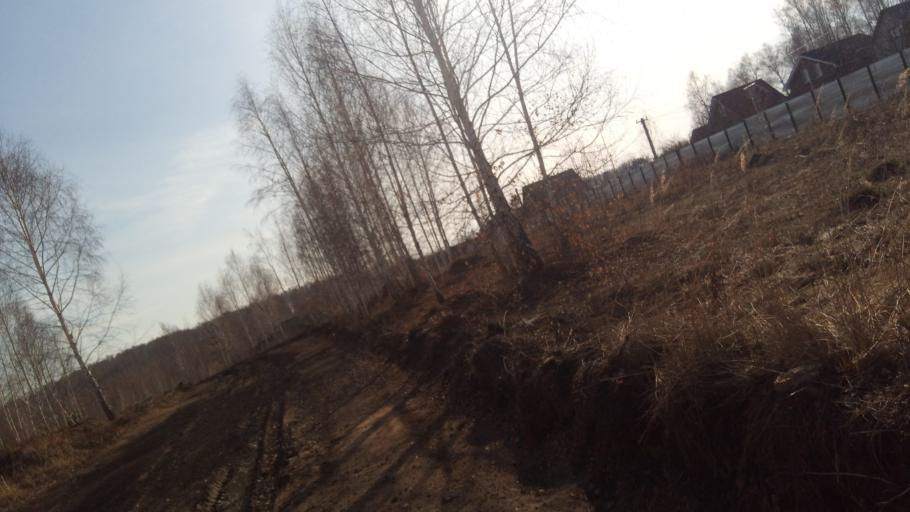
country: RU
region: Chelyabinsk
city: Sargazy
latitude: 55.1217
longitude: 61.2431
